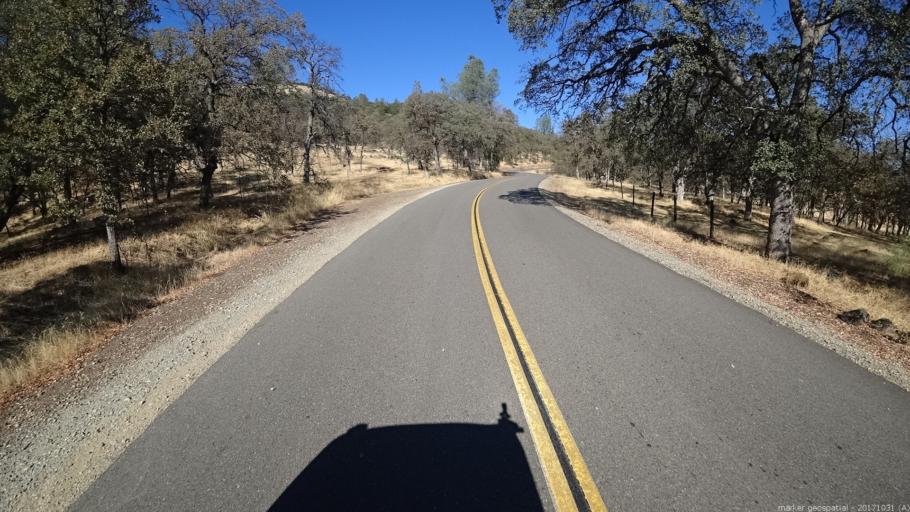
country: US
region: California
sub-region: Shasta County
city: Shingletown
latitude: 40.4440
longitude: -121.9979
